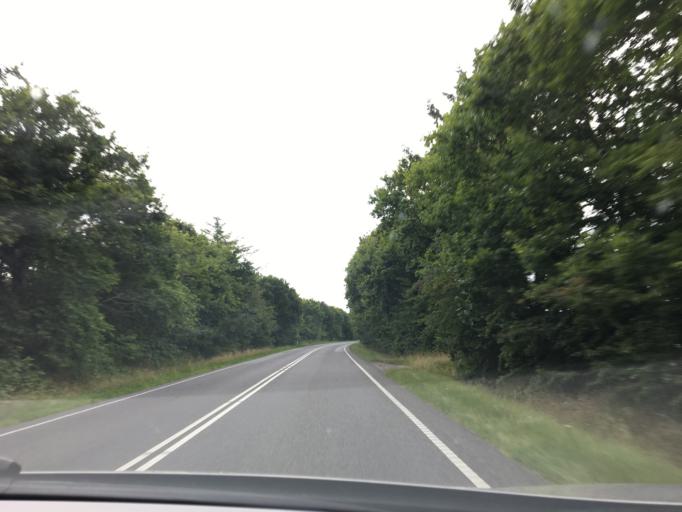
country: DK
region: South Denmark
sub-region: Varde Kommune
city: Oksbol
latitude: 55.7042
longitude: 8.3116
